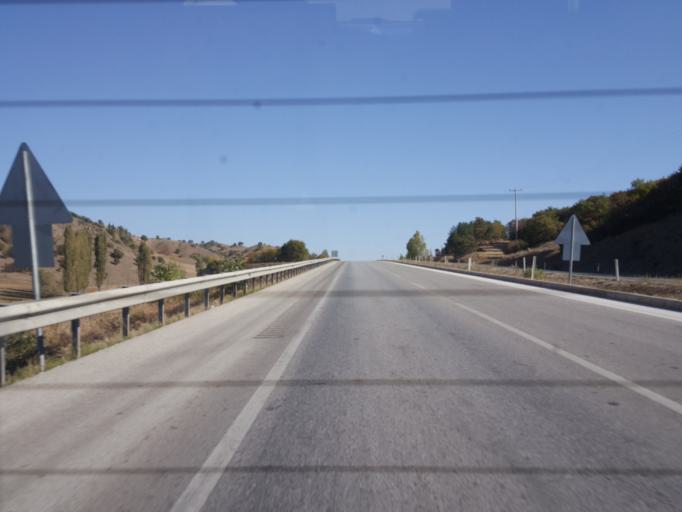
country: TR
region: Corum
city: Alaca
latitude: 40.2775
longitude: 34.6432
